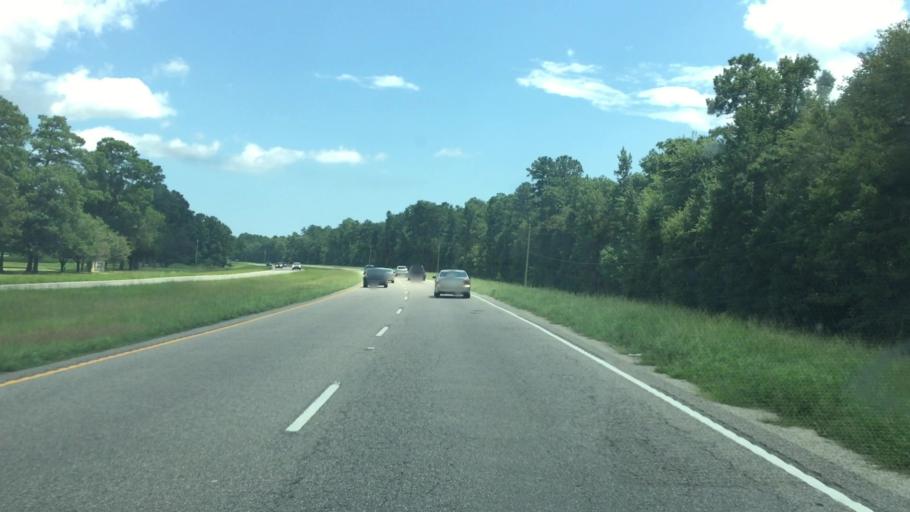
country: US
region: South Carolina
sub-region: Horry County
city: North Myrtle Beach
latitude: 33.9188
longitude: -78.7237
